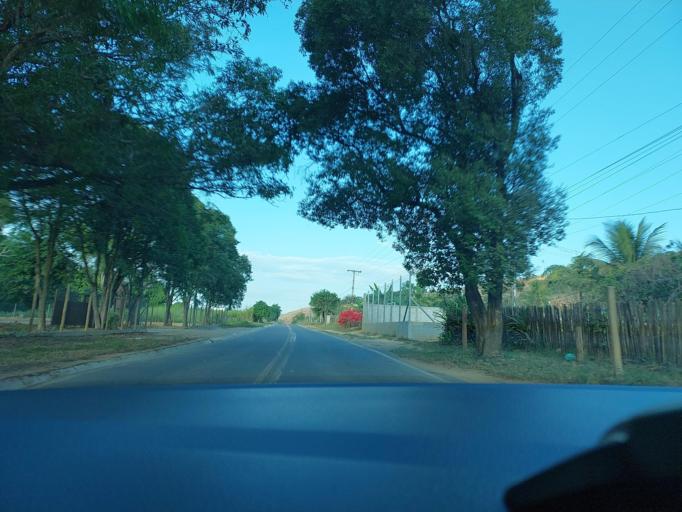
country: BR
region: Minas Gerais
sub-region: Muriae
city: Muriae
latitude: -21.1165
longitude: -42.4315
